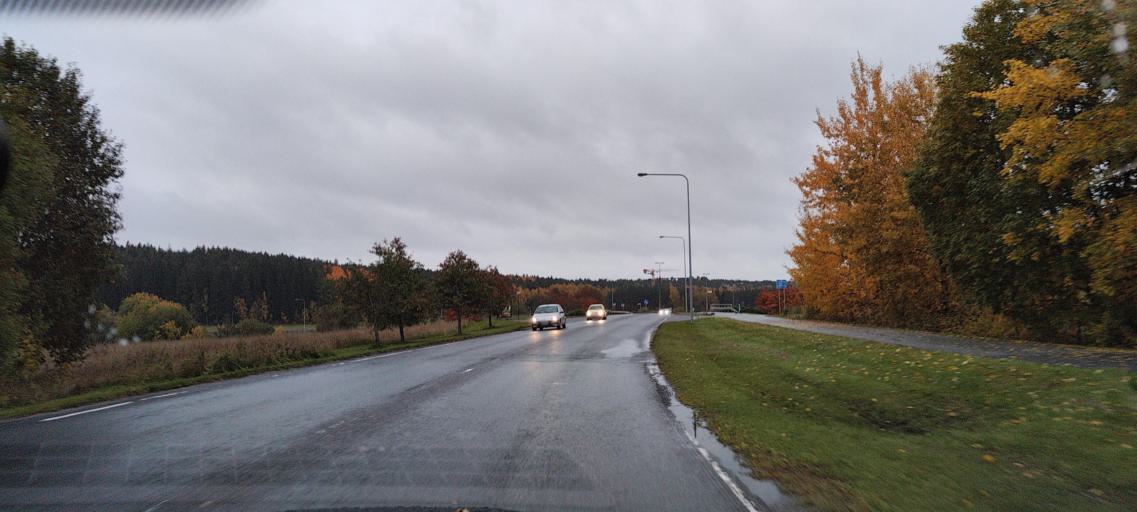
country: FI
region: Varsinais-Suomi
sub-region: Turku
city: Kaarina
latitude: 60.4598
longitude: 22.3352
